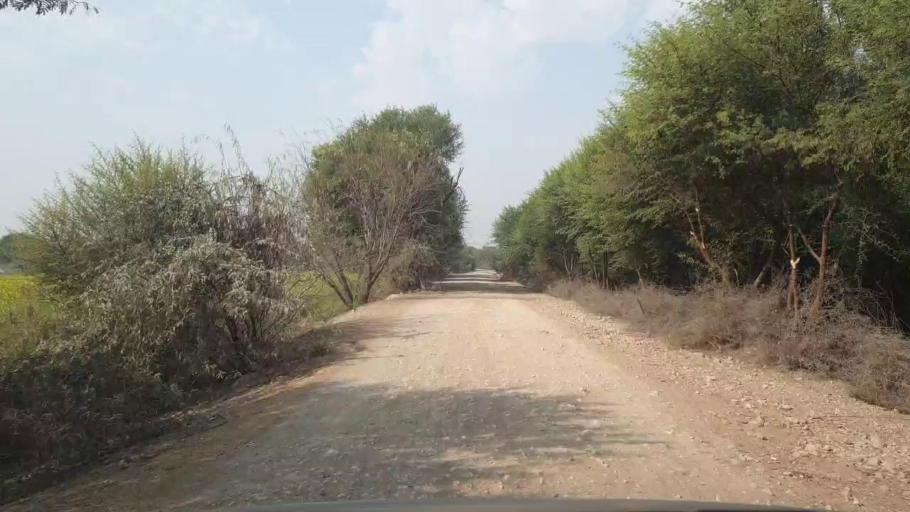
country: PK
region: Sindh
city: Hala
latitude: 25.7724
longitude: 68.4412
